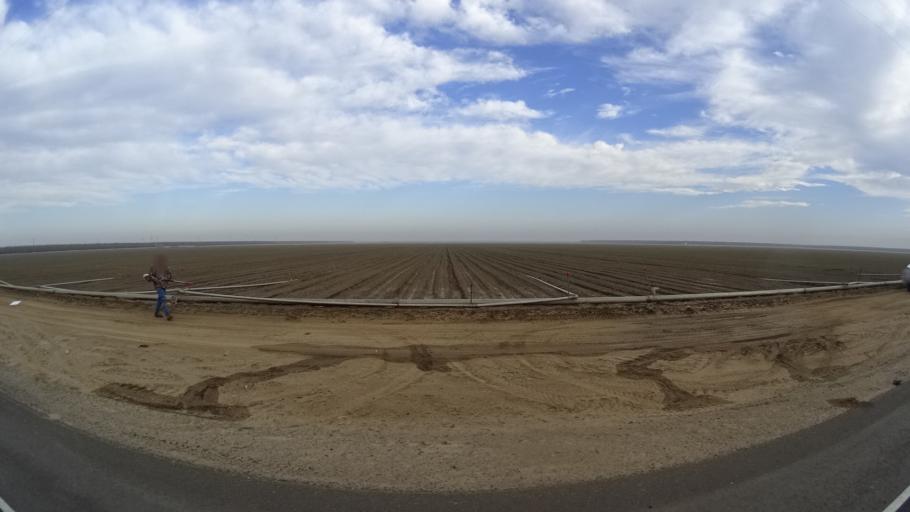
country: US
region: California
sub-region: Kern County
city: Rosedale
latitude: 35.4198
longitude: -119.2218
